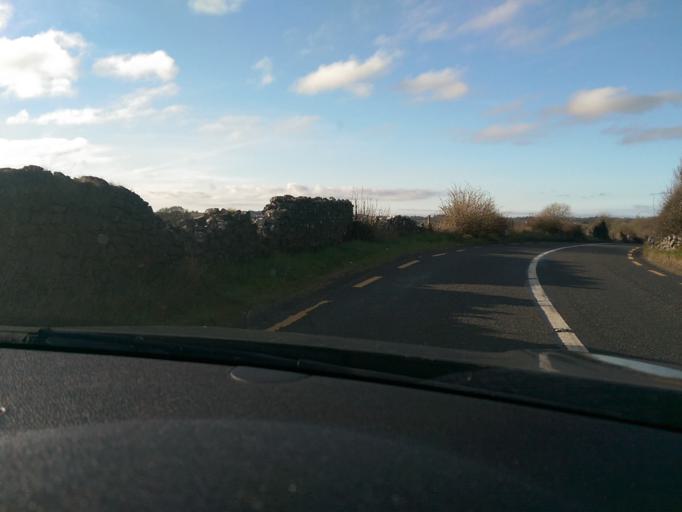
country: IE
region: Connaught
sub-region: Roscommon
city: Roscommon
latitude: 53.7657
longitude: -8.2493
